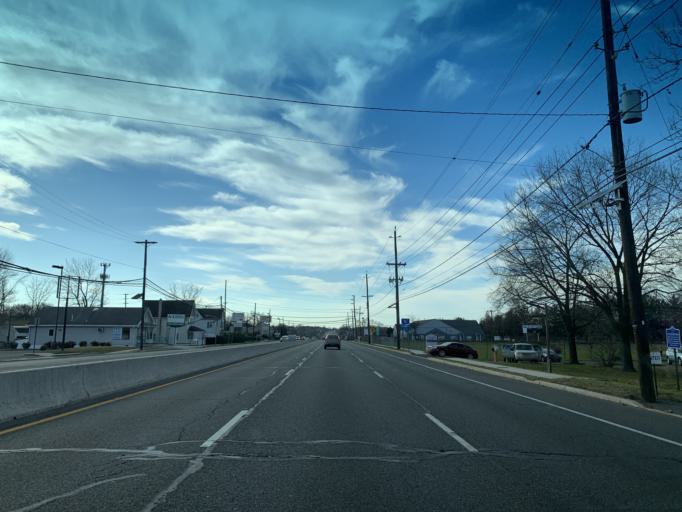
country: US
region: New Jersey
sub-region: Burlington County
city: Delanco
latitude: 40.0190
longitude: -74.9483
